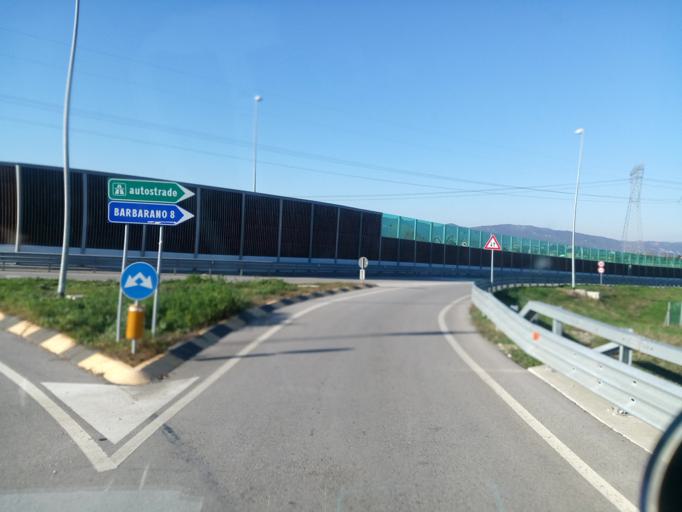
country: IT
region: Veneto
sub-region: Provincia di Vicenza
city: Albettone
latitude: 45.3798
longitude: 11.6114
